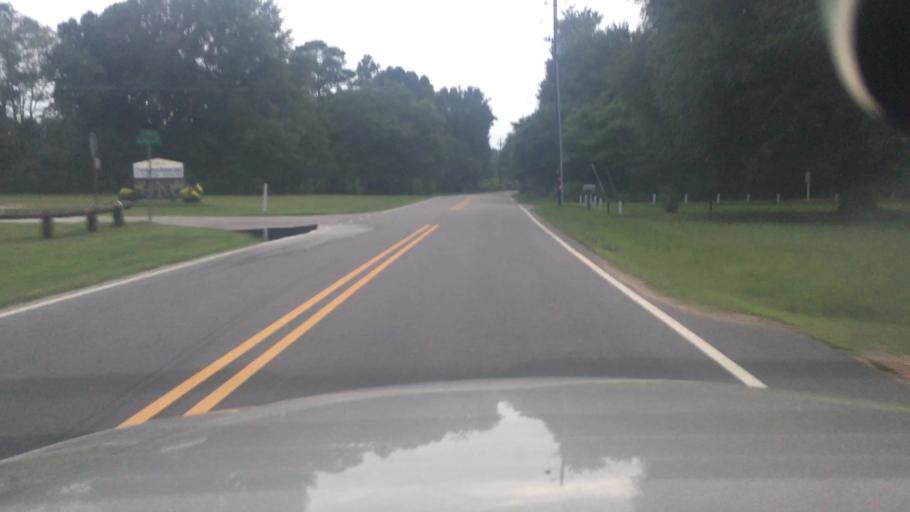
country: US
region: North Carolina
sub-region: Cumberland County
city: Hope Mills
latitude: 34.9657
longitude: -78.9304
